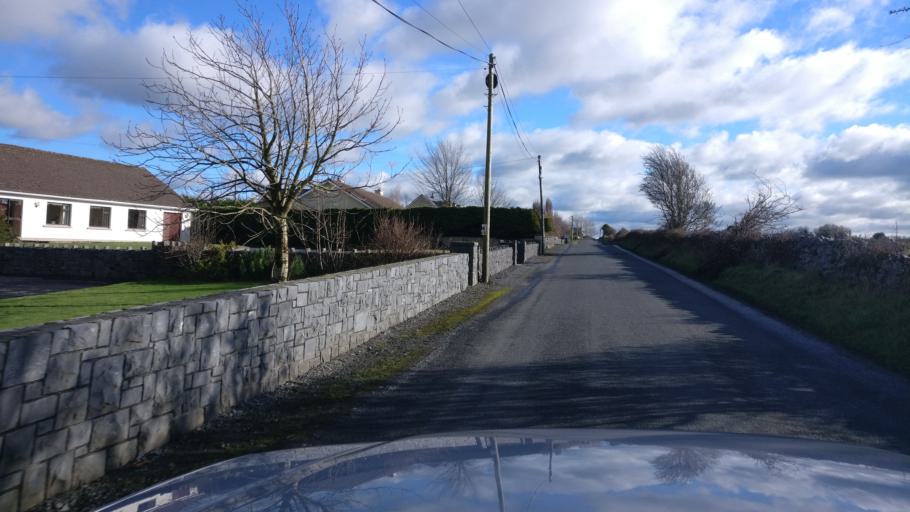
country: IE
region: Connaught
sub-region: County Galway
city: Oranmore
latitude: 53.2524
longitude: -8.8488
